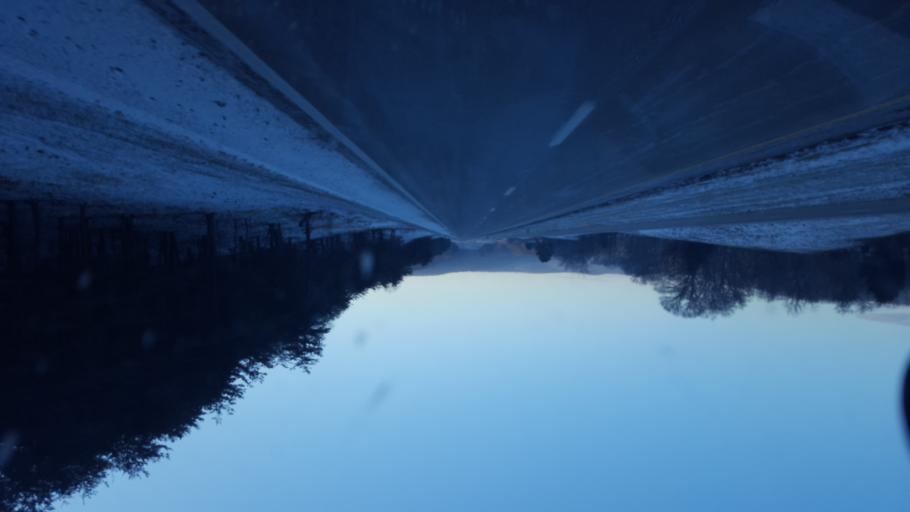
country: US
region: Ohio
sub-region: Adams County
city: Peebles
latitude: 38.9847
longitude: -83.3210
